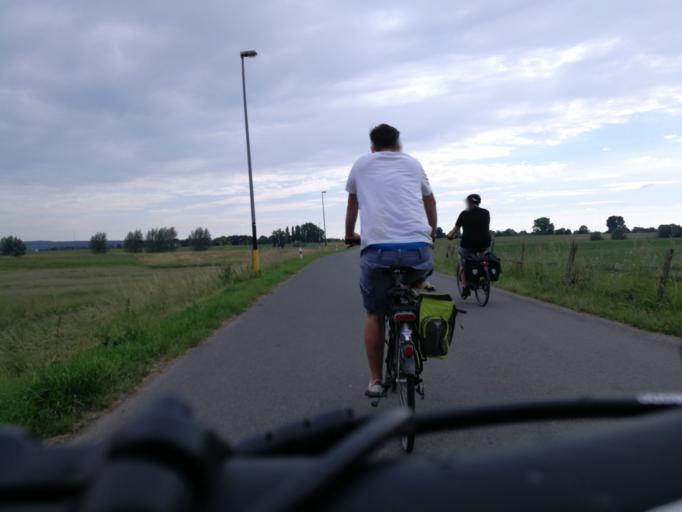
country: DE
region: North Rhine-Westphalia
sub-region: Regierungsbezirk Dusseldorf
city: Kleve
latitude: 51.8347
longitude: 6.1116
